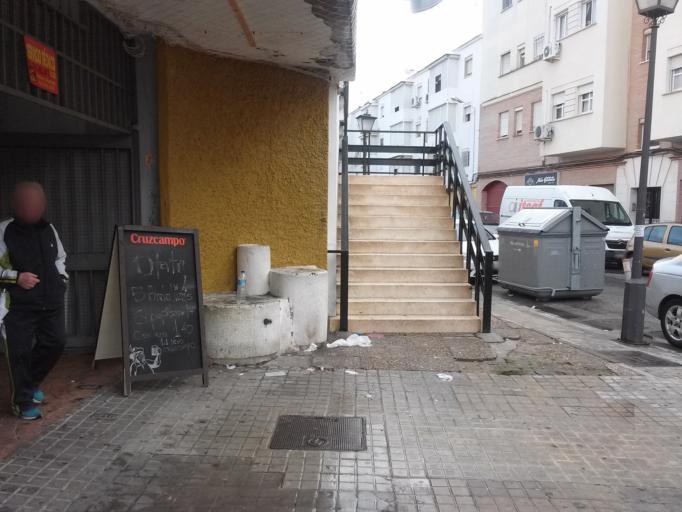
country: ES
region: Andalusia
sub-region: Provincia de Sevilla
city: Sevilla
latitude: 37.4256
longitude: -5.9845
